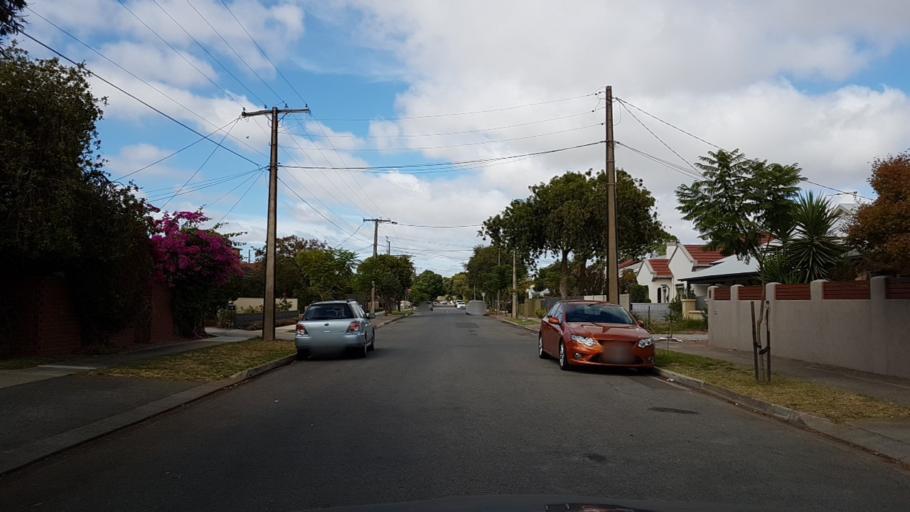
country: AU
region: South Australia
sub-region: Marion
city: South Plympton
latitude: -34.9694
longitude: 138.5530
